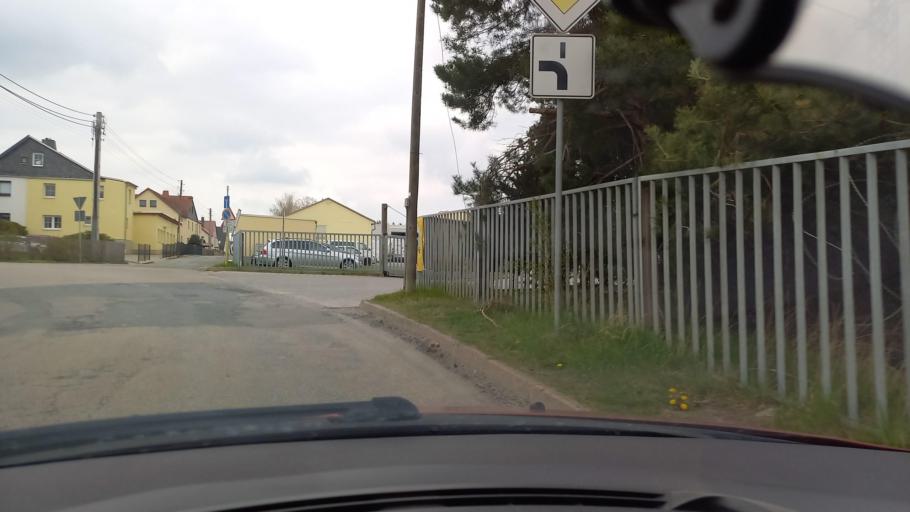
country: DE
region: Saxony
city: Wilkau-Hasslau
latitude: 50.6725
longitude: 12.4975
